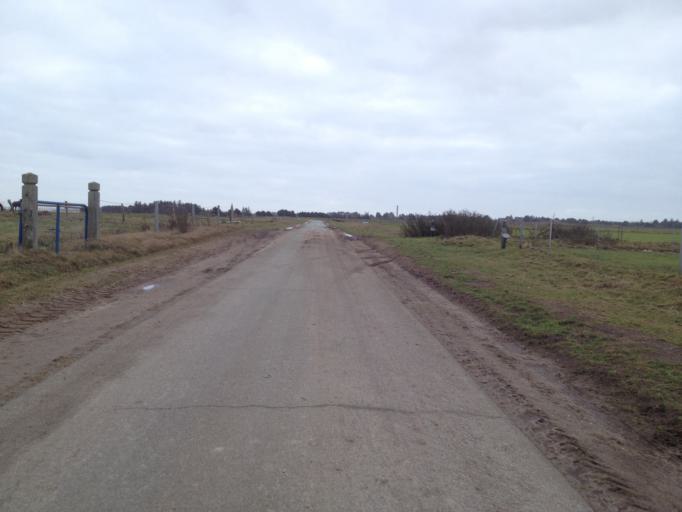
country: DE
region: Schleswig-Holstein
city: Nebel
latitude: 54.6613
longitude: 8.3480
